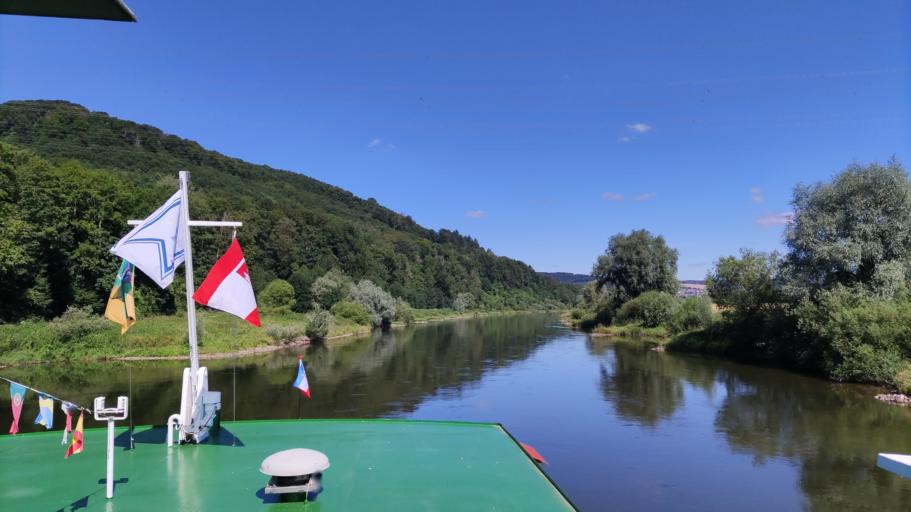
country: DE
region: North Rhine-Westphalia
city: Beverungen
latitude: 51.6407
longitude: 9.3782
